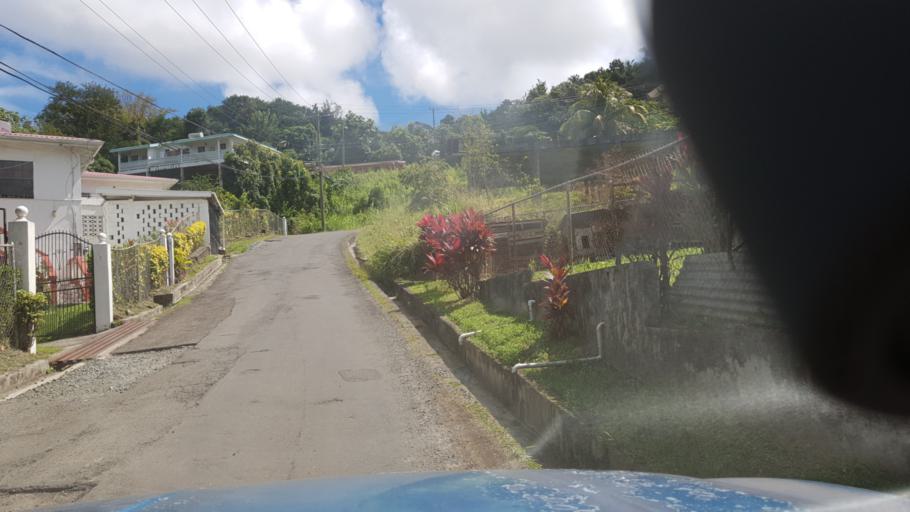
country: LC
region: Gros-Islet
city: Gros Islet
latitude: 14.0445
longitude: -60.9559
